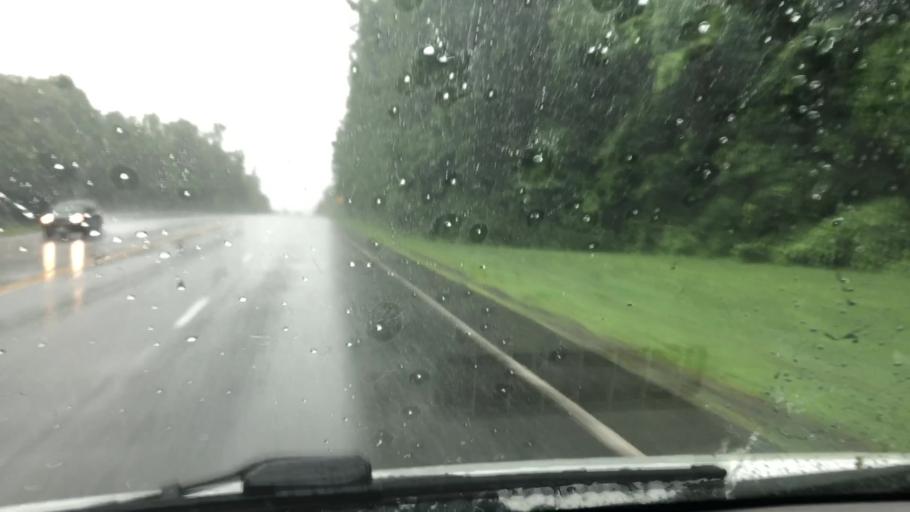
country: US
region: Massachusetts
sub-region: Berkshire County
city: Adams
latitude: 42.5896
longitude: -73.1467
